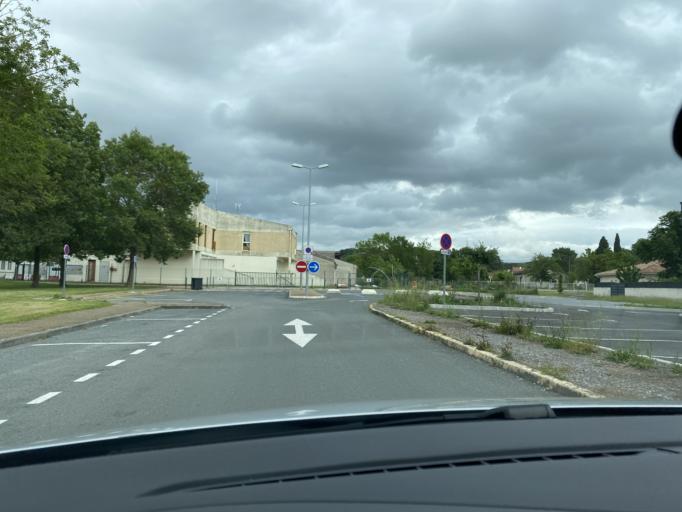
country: FR
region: Midi-Pyrenees
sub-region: Departement du Tarn
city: Saix
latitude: 43.5832
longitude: 2.1799
